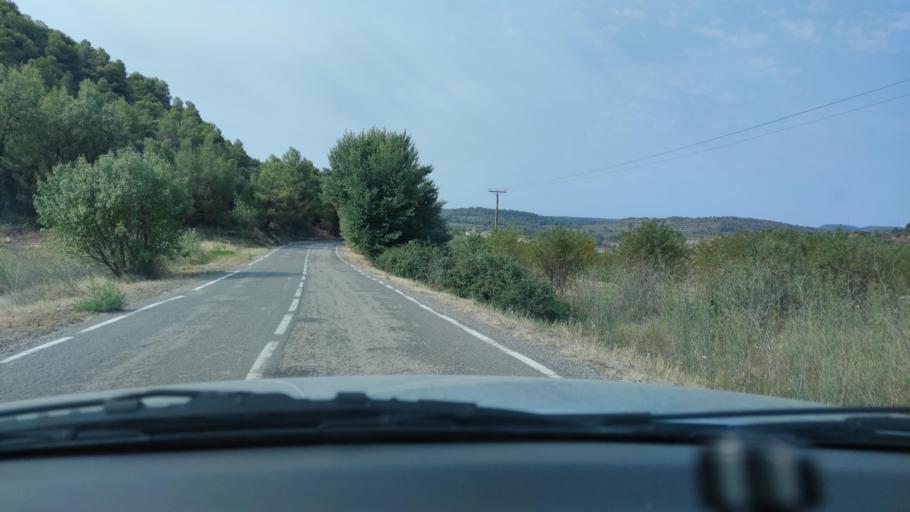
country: ES
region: Catalonia
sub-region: Provincia de Lleida
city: Juncosa
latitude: 41.4329
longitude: 0.8622
